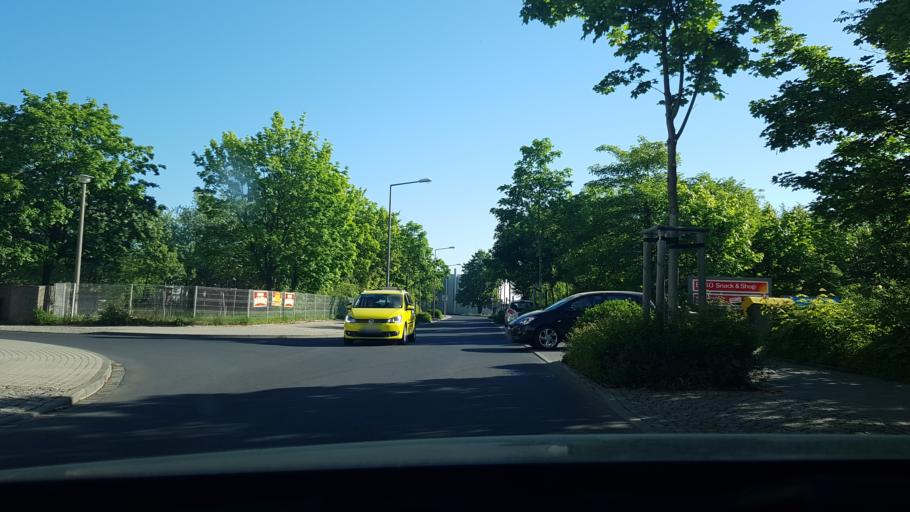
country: DE
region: Saxony
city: Heidenau
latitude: 51.0057
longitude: 13.8064
